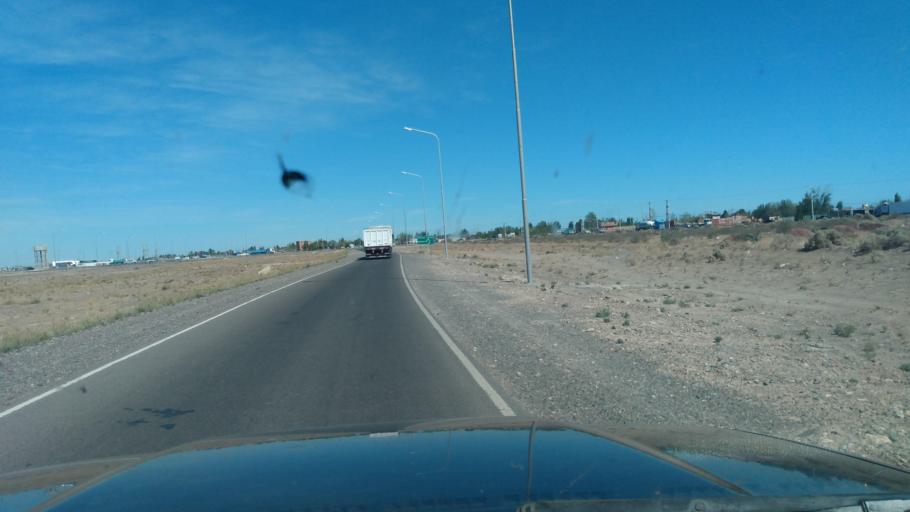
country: AR
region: Neuquen
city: Neuquen
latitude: -38.9126
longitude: -68.1168
